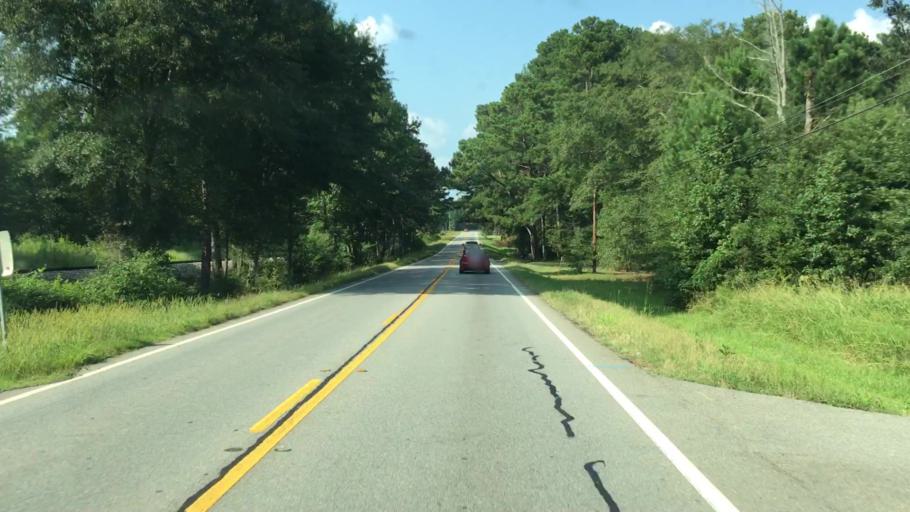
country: US
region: Georgia
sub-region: Walton County
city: Monroe
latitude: 33.7474
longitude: -83.7027
